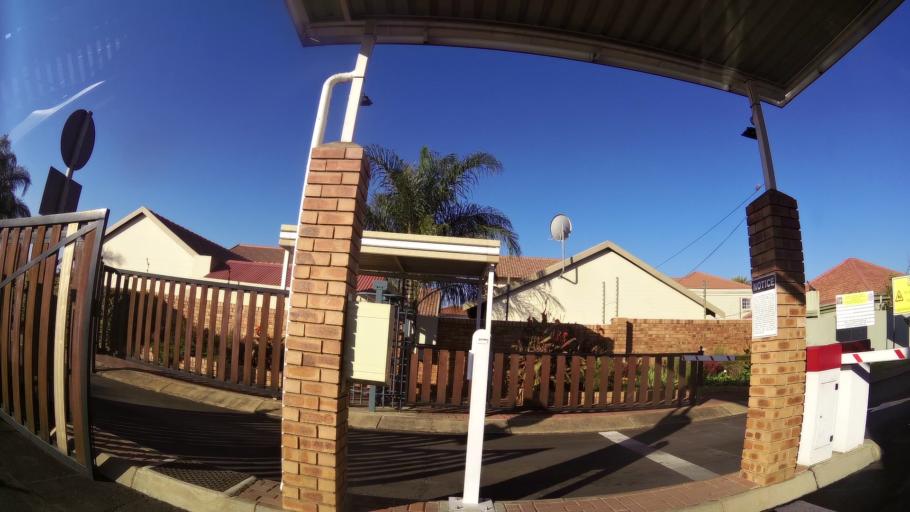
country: ZA
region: Gauteng
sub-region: City of Tshwane Metropolitan Municipality
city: Centurion
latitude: -25.8797
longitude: 28.1499
